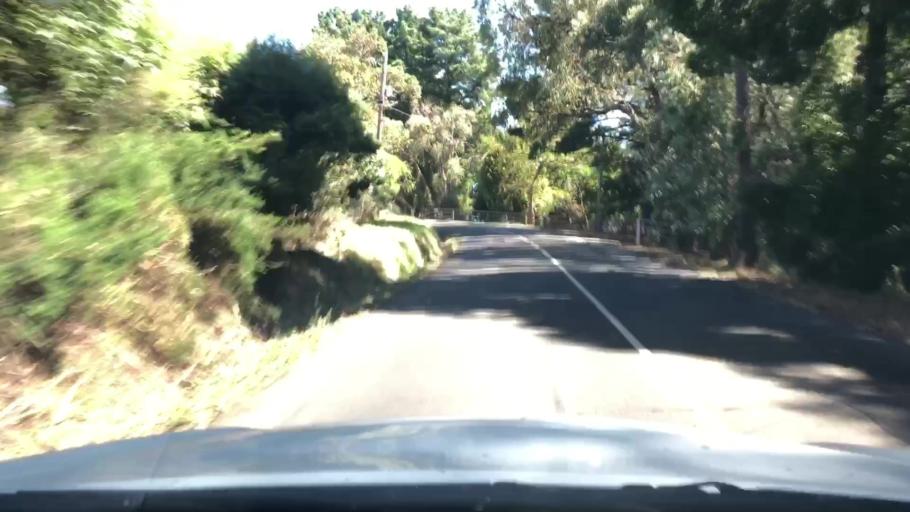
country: AU
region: Victoria
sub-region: Yarra Ranges
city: Macclesfield
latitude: -37.8997
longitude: 145.4697
